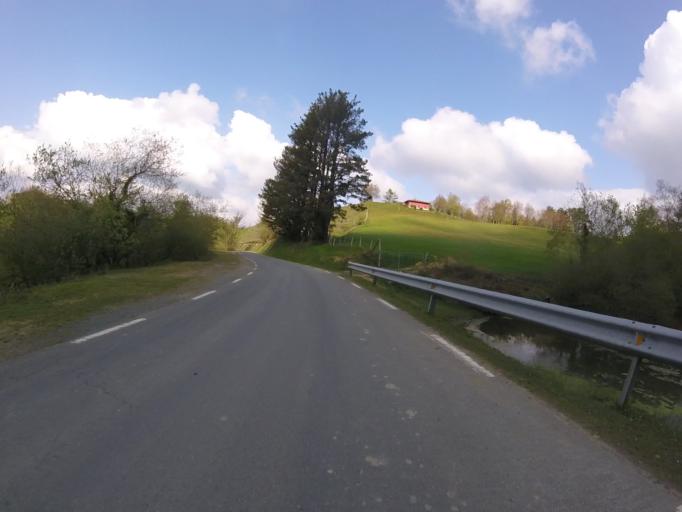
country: ES
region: Basque Country
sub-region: Provincia de Guipuzcoa
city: Azkoitia
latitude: 43.2093
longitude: -2.3237
